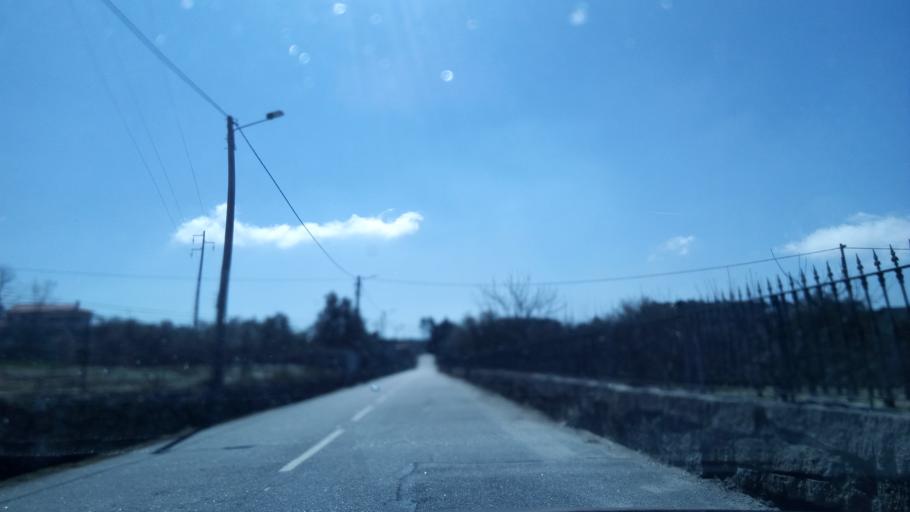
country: PT
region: Guarda
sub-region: Fornos de Algodres
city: Fornos de Algodres
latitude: 40.6500
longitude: -7.5342
